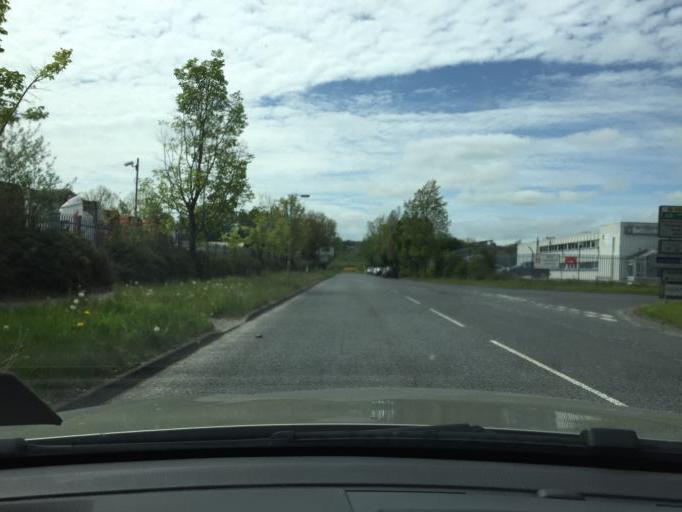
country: GB
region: Northern Ireland
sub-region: Newry and Mourne District
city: Newry
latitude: 54.2038
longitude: -6.3520
